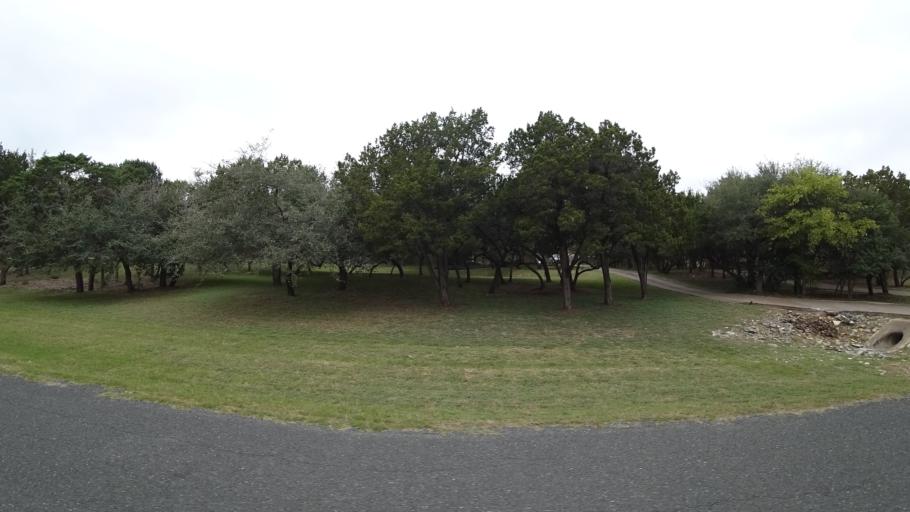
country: US
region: Texas
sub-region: Travis County
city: Barton Creek
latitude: 30.2525
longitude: -97.9066
